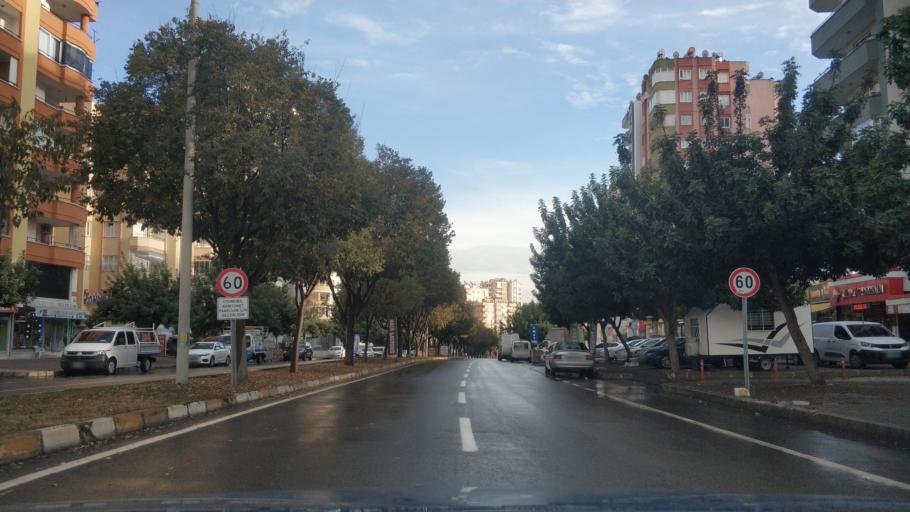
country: TR
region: Adana
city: Seyhan
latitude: 37.0396
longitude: 35.2760
